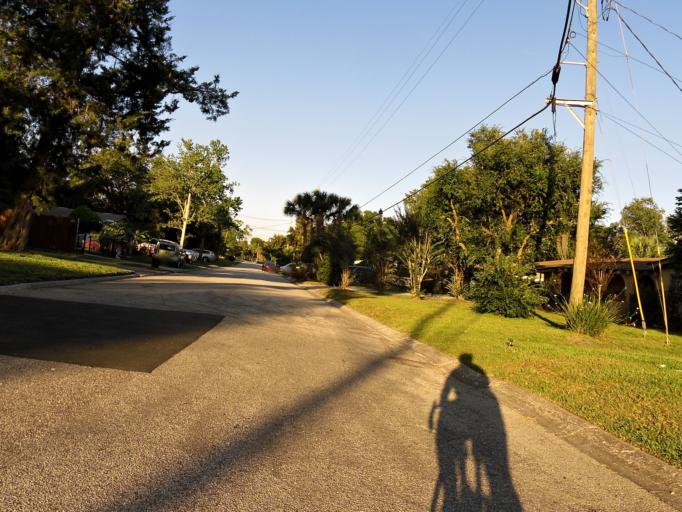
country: US
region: Florida
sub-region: Duval County
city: Jacksonville
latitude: 30.2317
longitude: -81.6151
